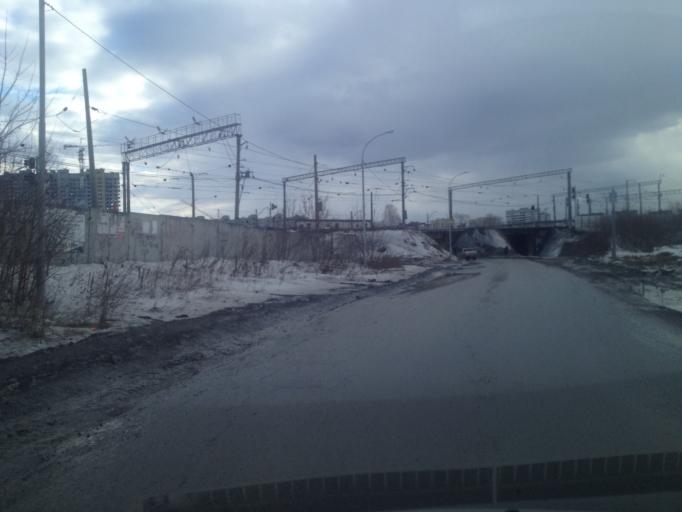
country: RU
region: Sverdlovsk
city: Yekaterinburg
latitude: 56.8595
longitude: 60.5817
